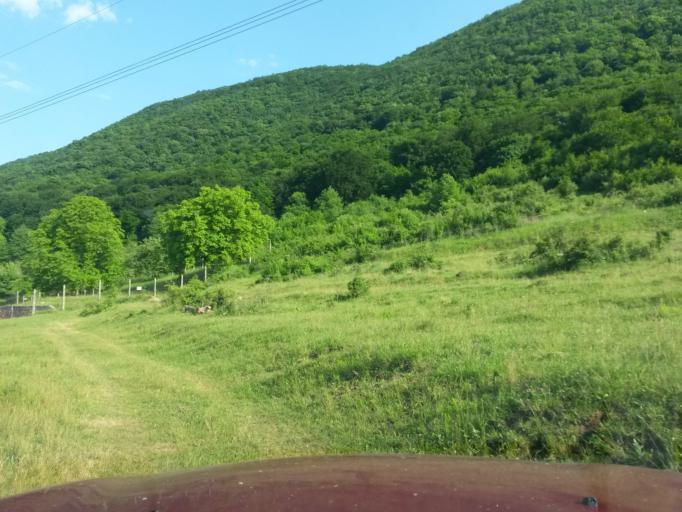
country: SK
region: Kosicky
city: Roznava
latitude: 48.5837
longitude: 20.6861
